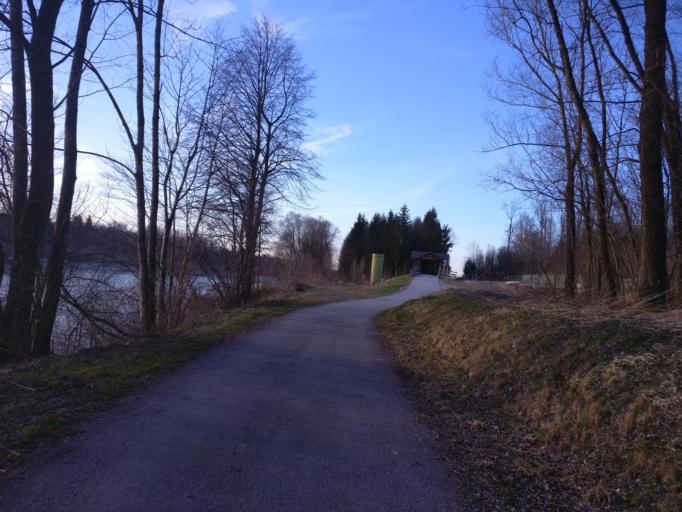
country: DE
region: Bavaria
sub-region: Upper Bavaria
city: Freilassing
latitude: 47.8495
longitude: 13.0081
